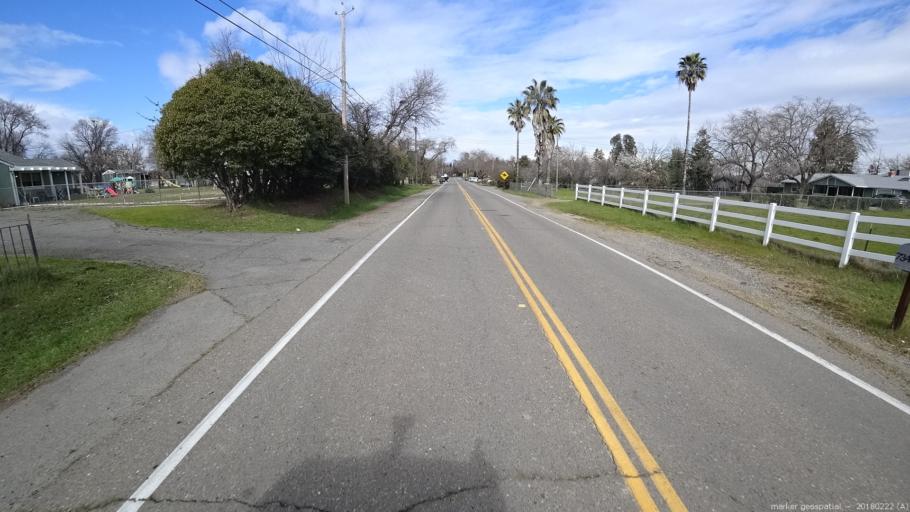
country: US
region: California
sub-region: Sacramento County
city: Rio Linda
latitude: 38.7008
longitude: -121.4106
